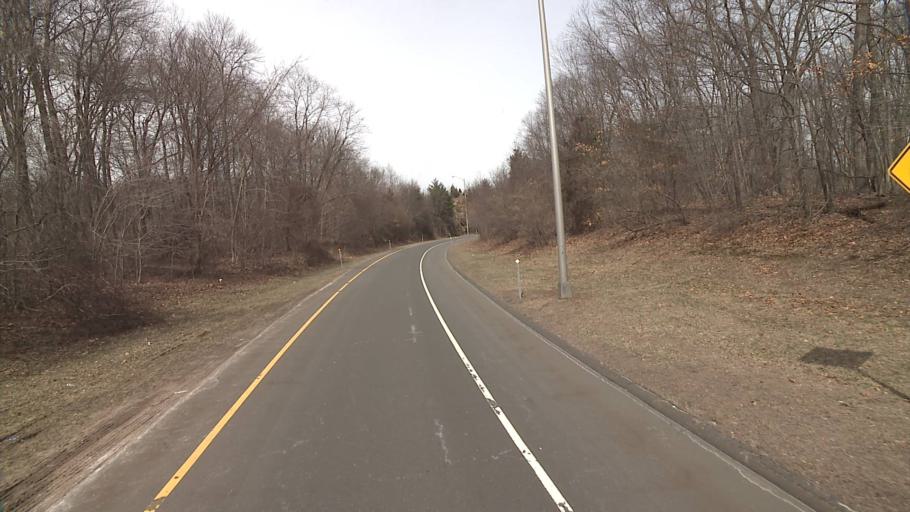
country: US
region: Connecticut
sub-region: Fairfield County
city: Trumbull
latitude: 41.2377
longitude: -73.1891
